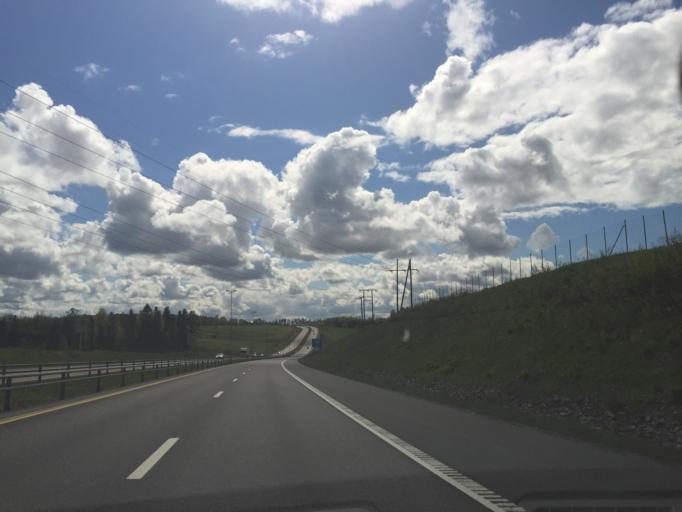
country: NO
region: Akershus
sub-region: Eidsvoll
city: Raholt
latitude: 60.2441
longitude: 11.1816
